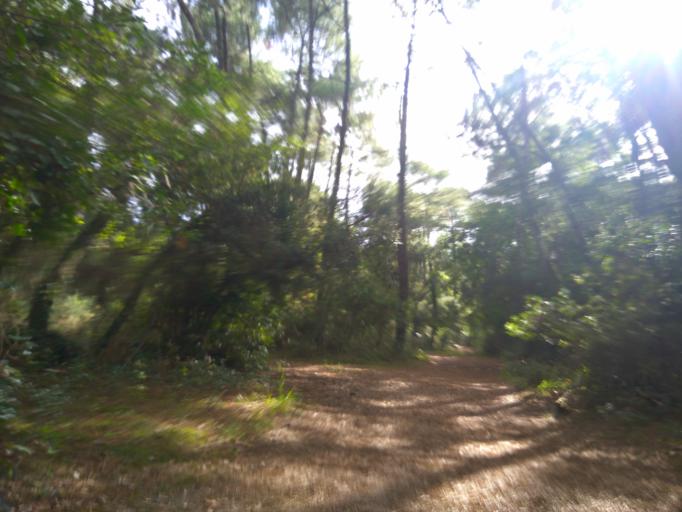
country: FR
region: Aquitaine
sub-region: Departement des Landes
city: Capbreton
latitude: 43.6310
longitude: -1.4428
